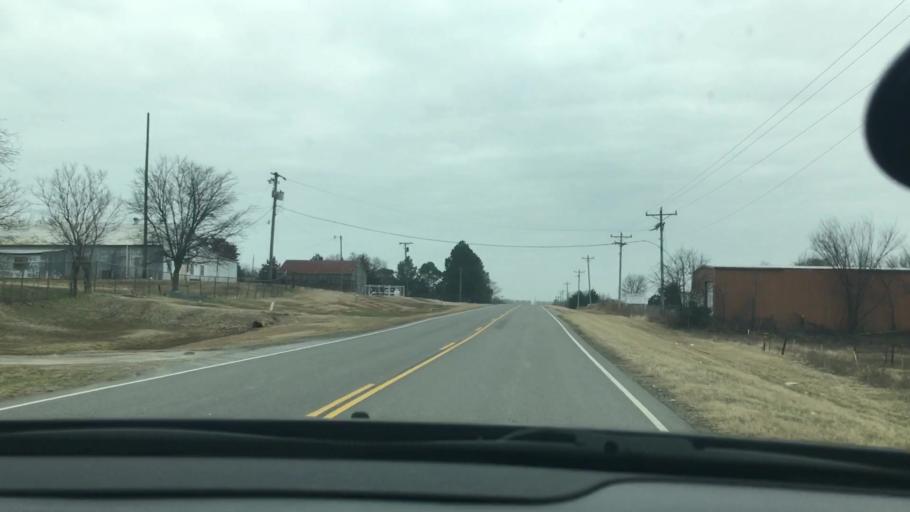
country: US
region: Oklahoma
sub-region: Carter County
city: Healdton
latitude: 34.2538
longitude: -97.4923
